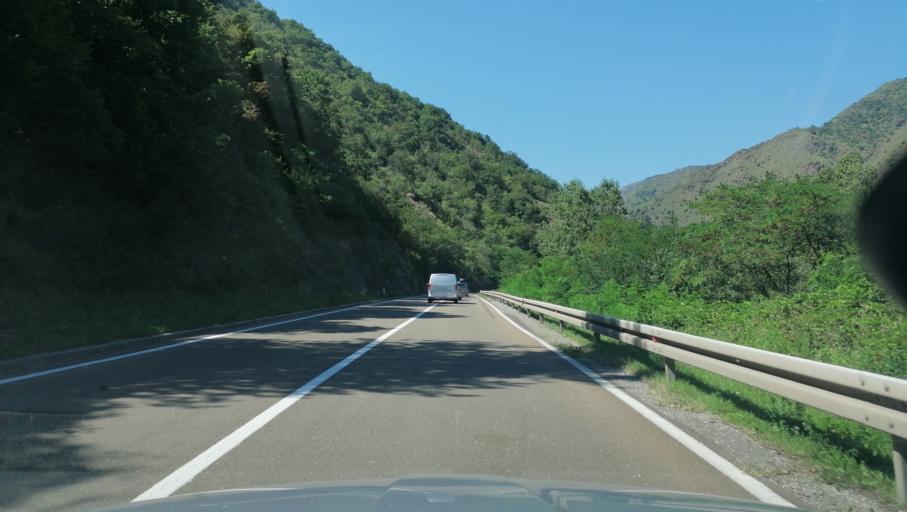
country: RS
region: Central Serbia
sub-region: Raski Okrug
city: Kraljevo
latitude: 43.5762
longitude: 20.5880
